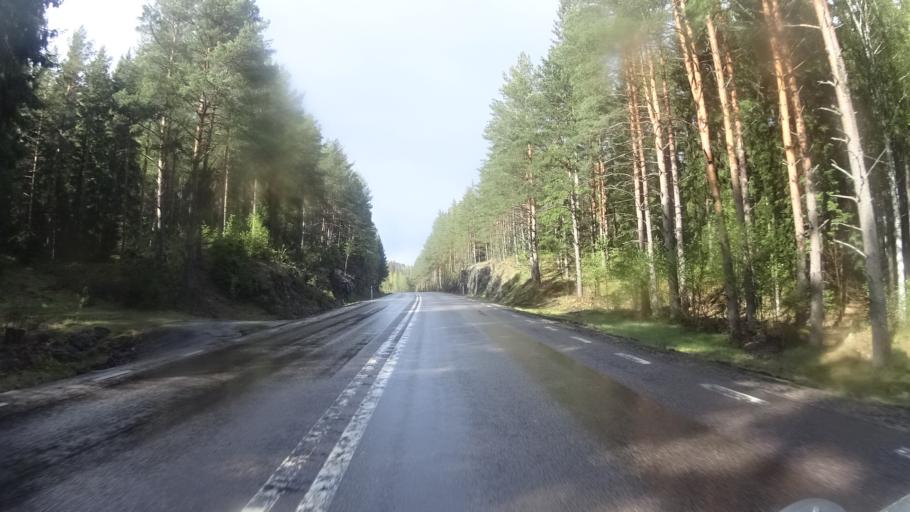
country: SE
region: OErebro
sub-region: Askersunds Kommun
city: Askersund
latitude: 58.7379
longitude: 14.7780
